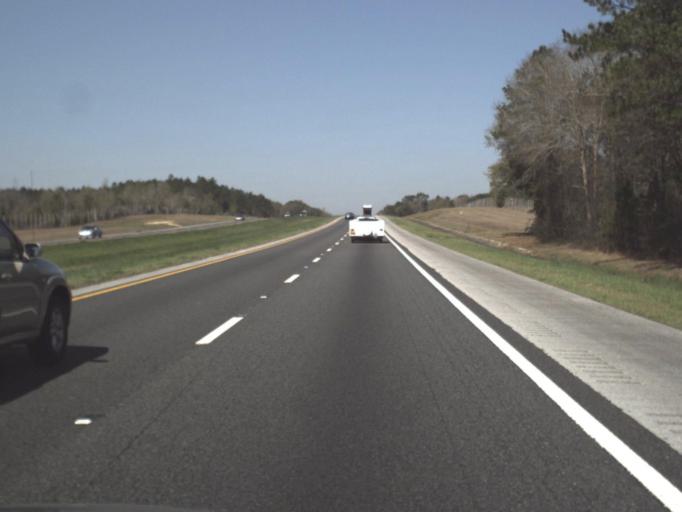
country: US
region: Florida
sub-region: Jackson County
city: Marianna
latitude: 30.6916
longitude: -85.1193
